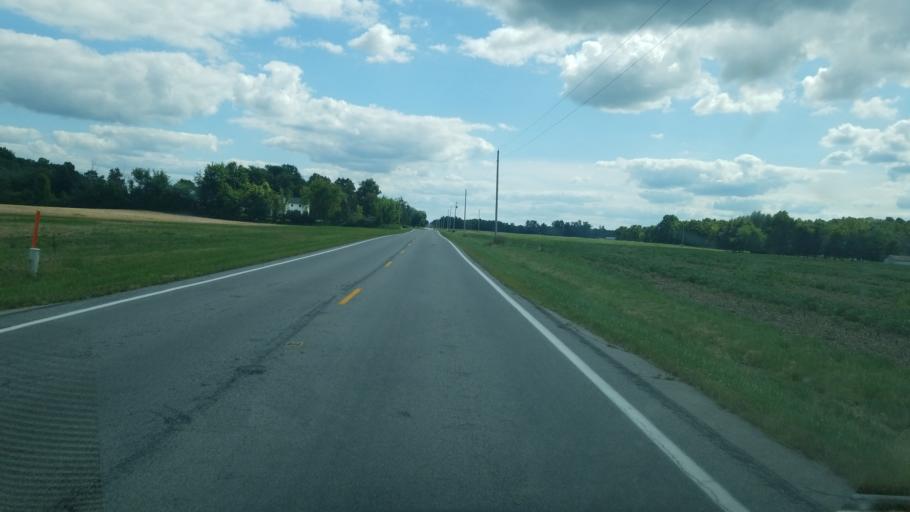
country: US
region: Ohio
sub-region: Allen County
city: Lima
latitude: 40.6761
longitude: -83.9758
